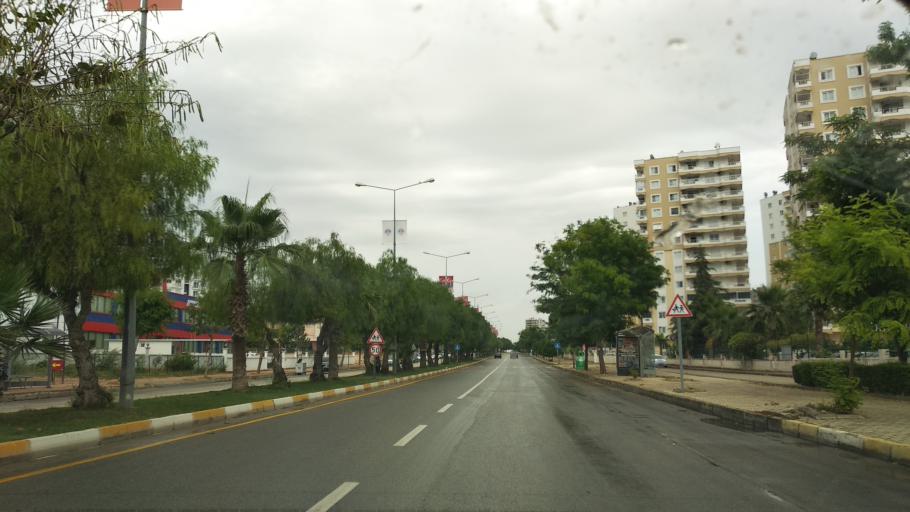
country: TR
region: Mersin
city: Mercin
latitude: 36.7940
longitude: 34.5825
